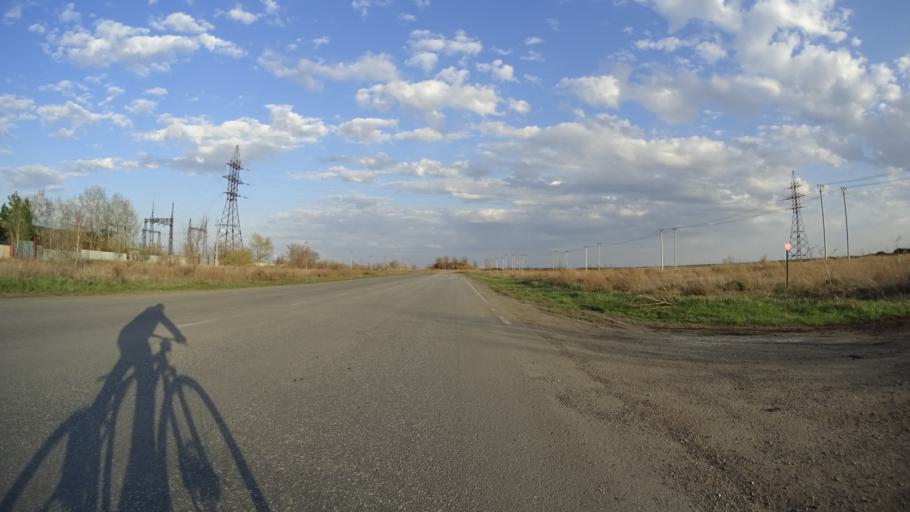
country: RU
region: Chelyabinsk
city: Troitsk
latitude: 54.0630
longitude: 61.5709
